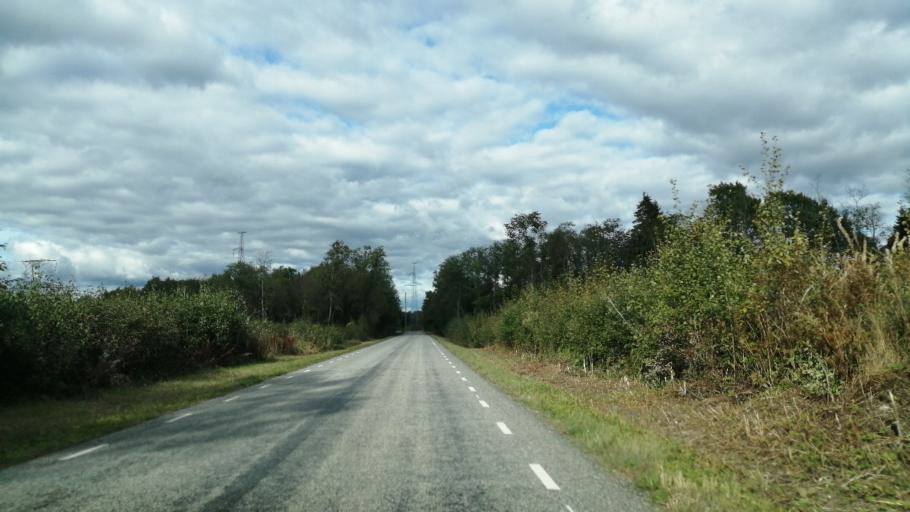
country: EE
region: Jaervamaa
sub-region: Tueri vald
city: Tueri
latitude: 58.7942
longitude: 25.4793
